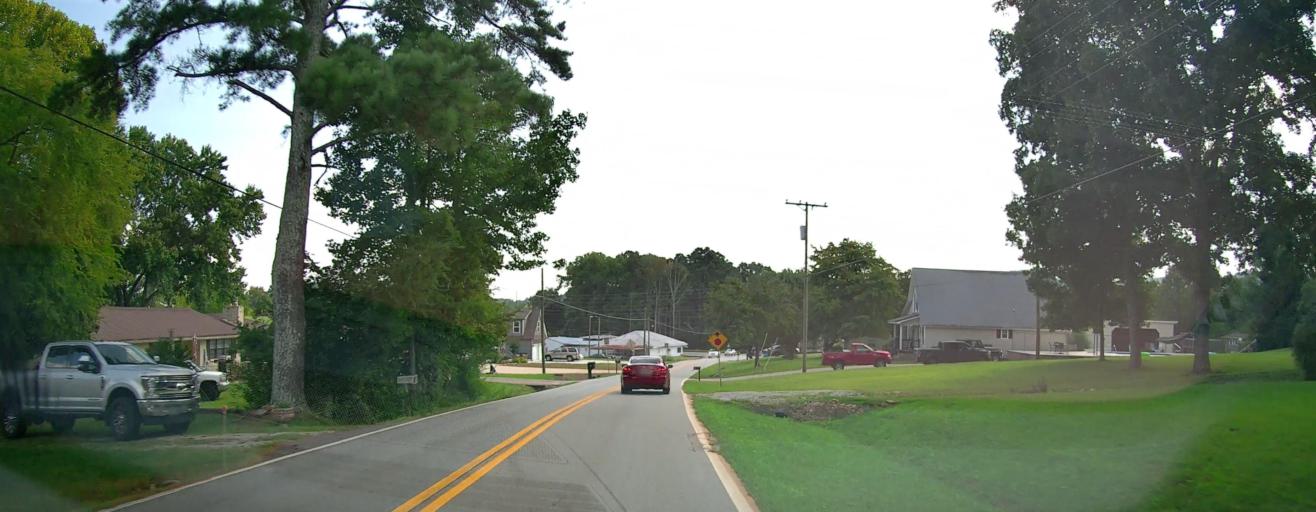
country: US
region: Georgia
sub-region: Catoosa County
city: Ringgold
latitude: 34.9134
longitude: -85.0865
